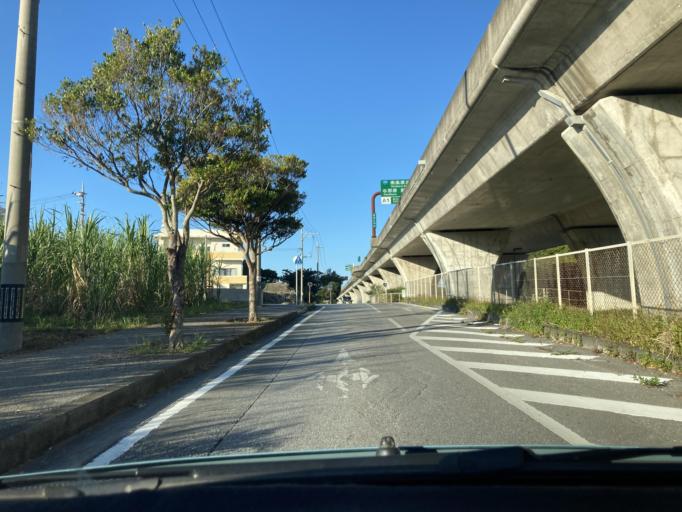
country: JP
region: Okinawa
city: Tomigusuku
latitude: 26.1893
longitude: 127.7381
